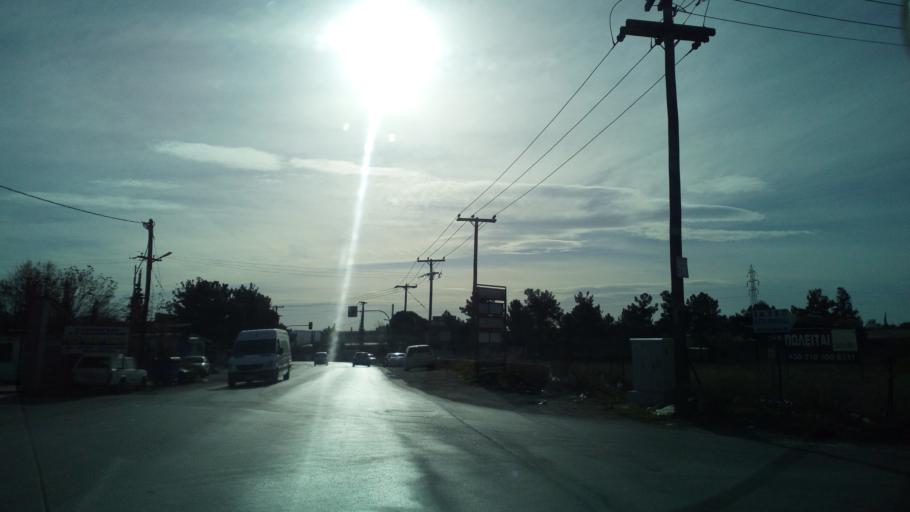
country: GR
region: Central Macedonia
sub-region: Nomos Thessalonikis
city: Efkarpia
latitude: 40.6922
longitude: 22.9345
